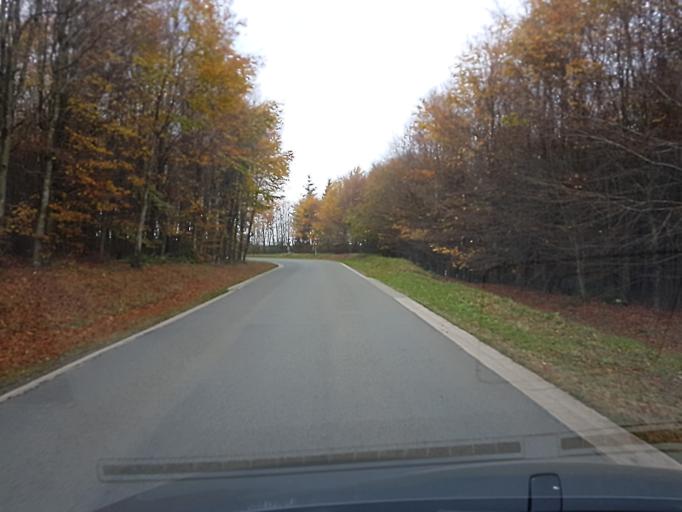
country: BE
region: Wallonia
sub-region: Province de Liege
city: Malmedy
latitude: 50.4693
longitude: 6.0310
